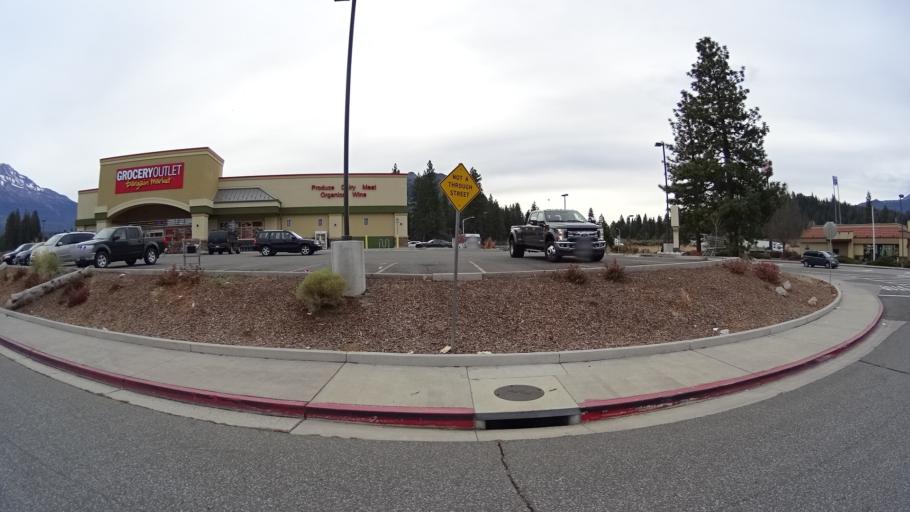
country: US
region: California
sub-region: Siskiyou County
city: Weed
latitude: 41.3983
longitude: -122.3772
